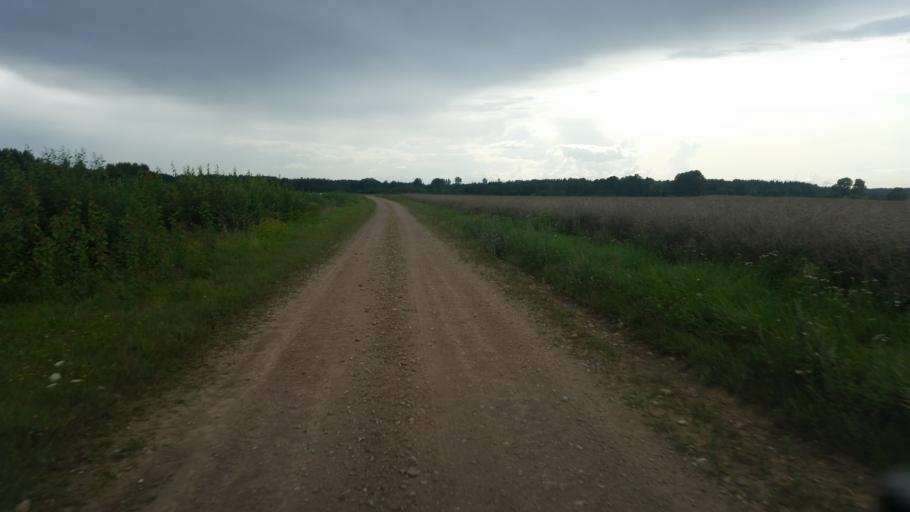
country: LV
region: Vecumnieki
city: Vecumnieki
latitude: 56.4502
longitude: 24.6427
